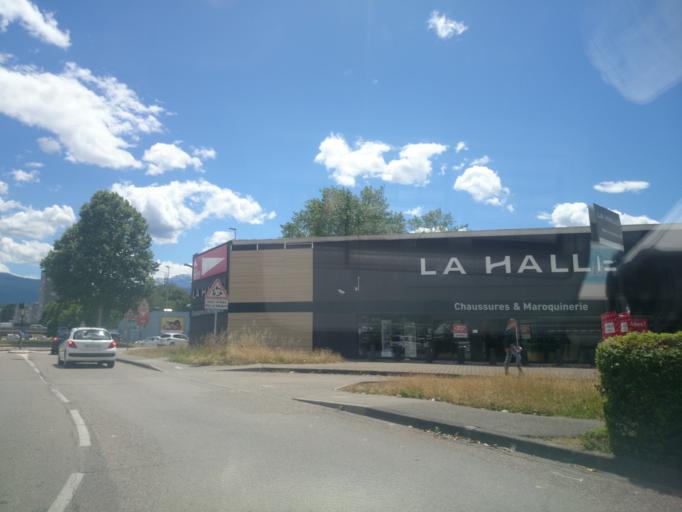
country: FR
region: Rhone-Alpes
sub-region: Departement de l'Isere
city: Seyssins
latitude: 45.1506
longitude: 5.6946
